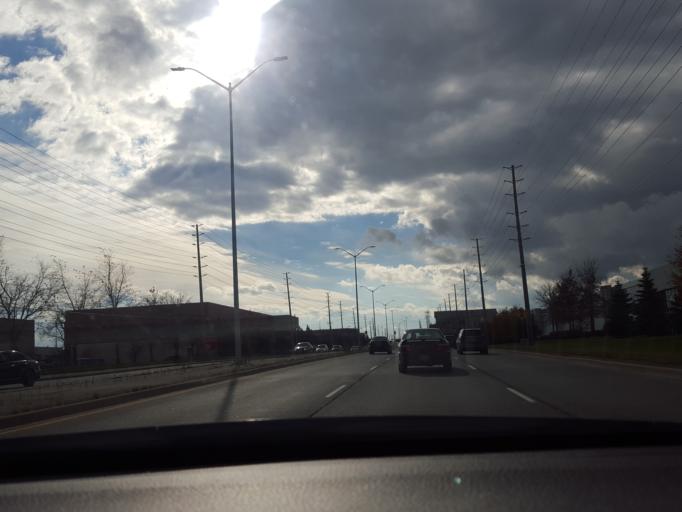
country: CA
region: Ontario
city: Brampton
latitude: 43.6543
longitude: -79.6971
